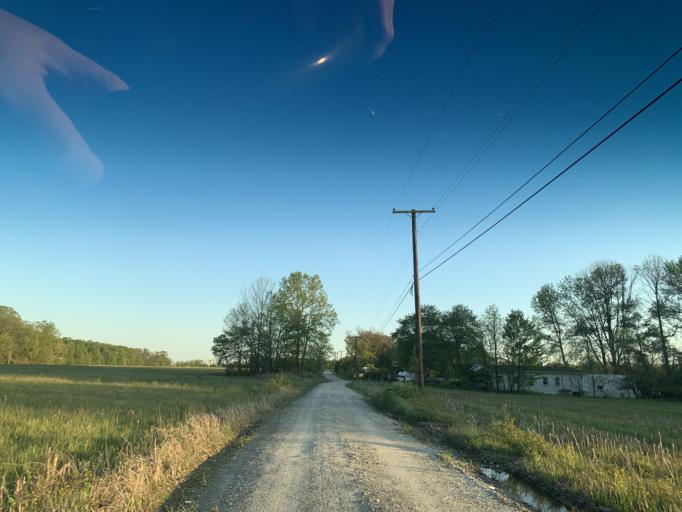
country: US
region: Maryland
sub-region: Harford County
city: Aberdeen
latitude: 39.5094
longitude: -76.1905
